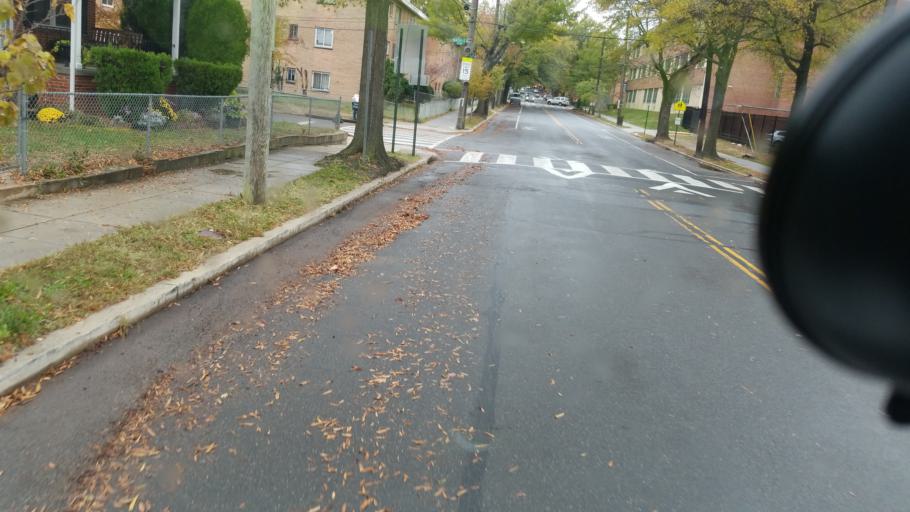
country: US
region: Maryland
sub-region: Prince George's County
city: Fairmount Heights
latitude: 38.9075
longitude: -76.9316
